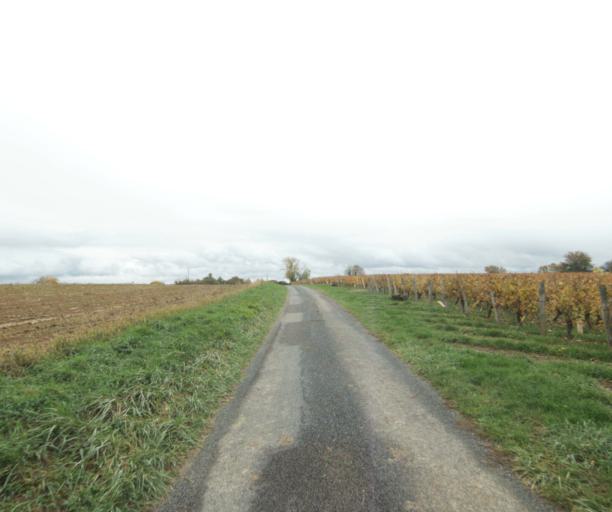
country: FR
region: Rhone-Alpes
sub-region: Departement de l'Ain
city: Pont-de-Vaux
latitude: 46.4698
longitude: 4.8784
